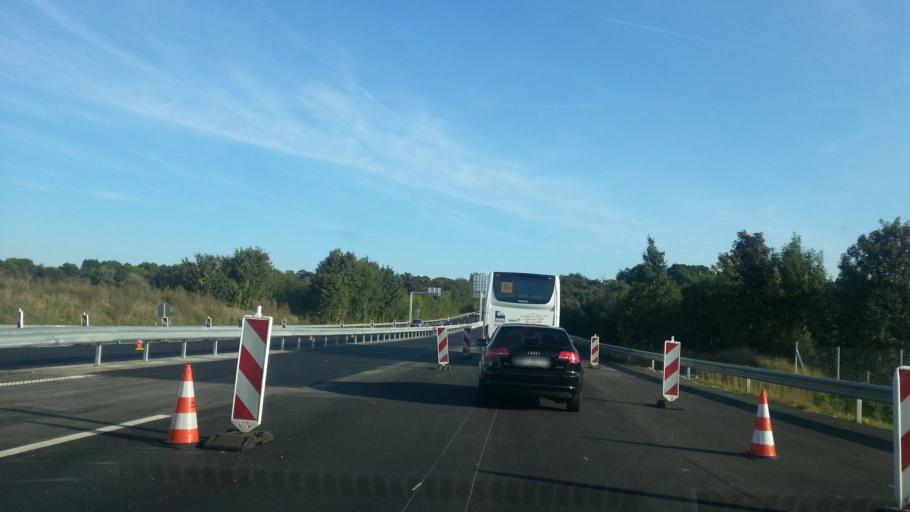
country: FR
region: Picardie
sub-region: Departement de l'Oise
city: Tille
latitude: 49.4593
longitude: 2.0888
